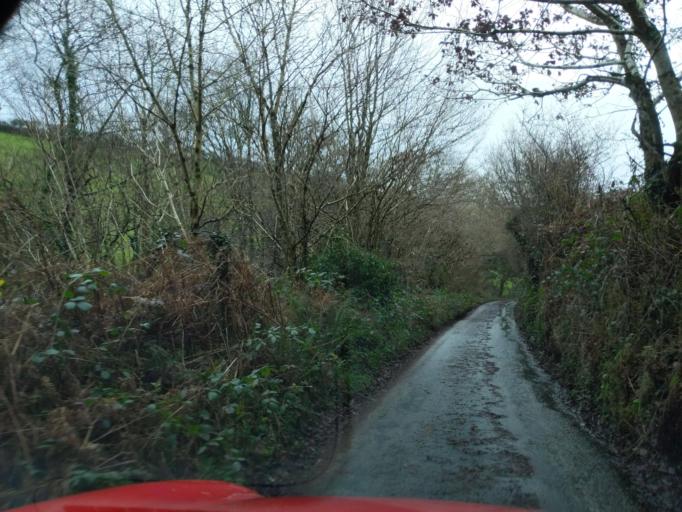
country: GB
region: England
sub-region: Cornwall
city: Duloe
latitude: 50.3478
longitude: -4.5179
